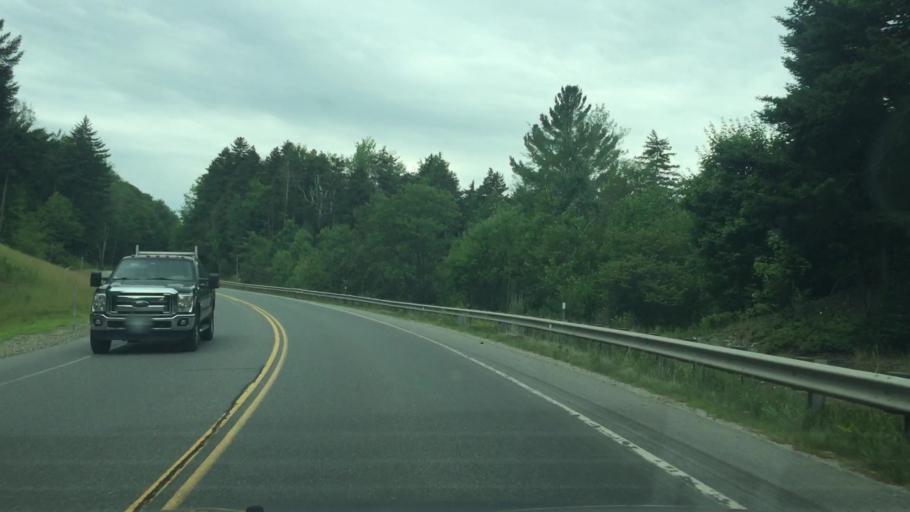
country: US
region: New Hampshire
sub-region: Grafton County
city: Deerfield
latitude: 44.2450
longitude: -71.6443
